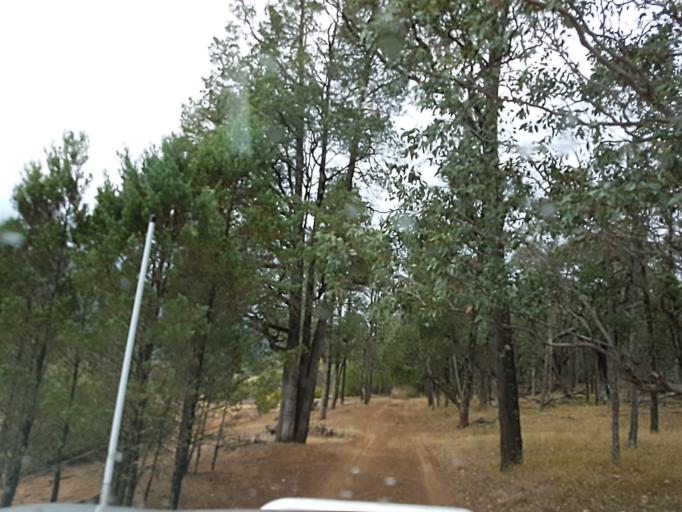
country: AU
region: New South Wales
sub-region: Snowy River
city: Jindabyne
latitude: -36.9487
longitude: 148.3982
